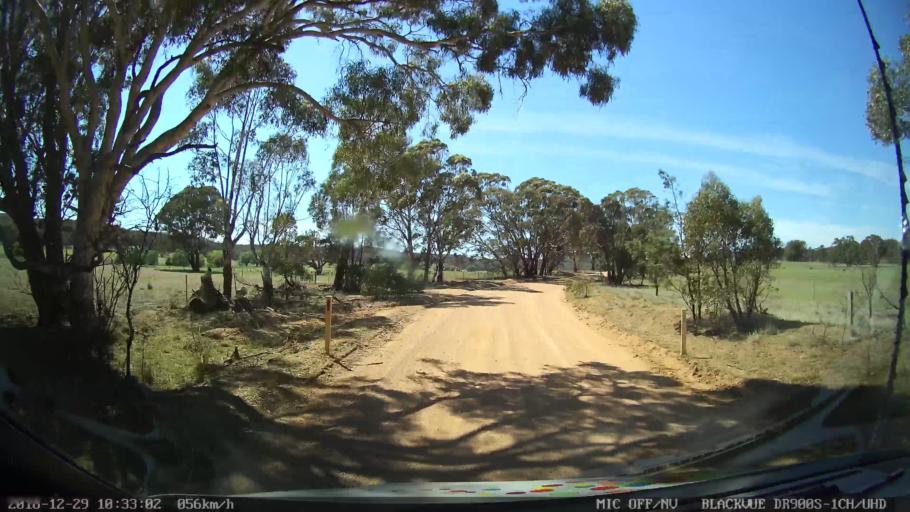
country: AU
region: New South Wales
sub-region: Yass Valley
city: Gundaroo
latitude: -34.9777
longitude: 149.4701
